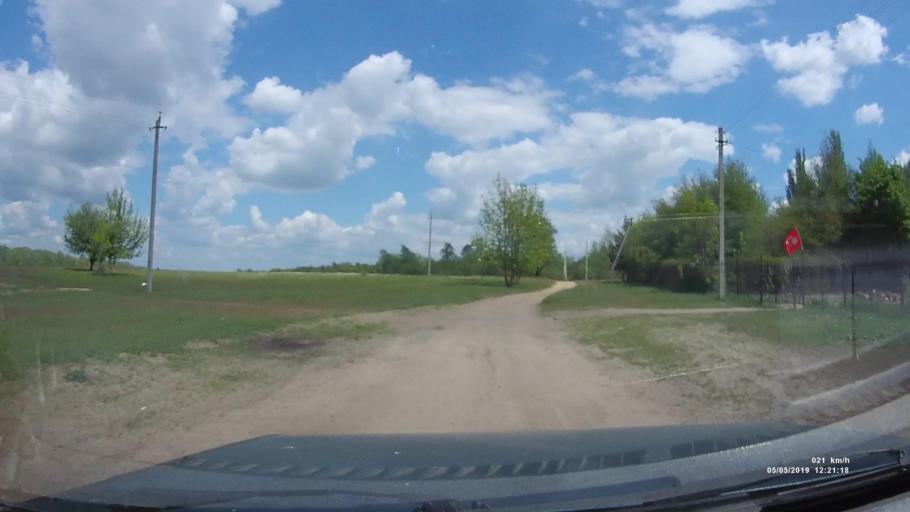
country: RU
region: Rostov
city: Konstantinovsk
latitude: 47.7546
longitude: 41.0370
